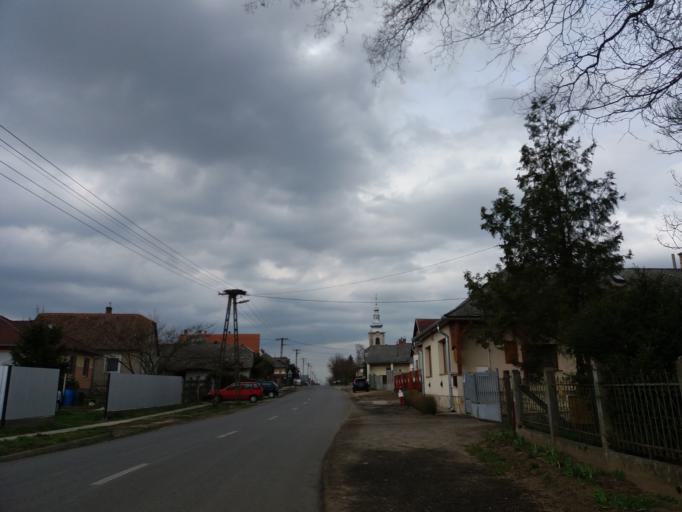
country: HU
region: Szabolcs-Szatmar-Bereg
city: Nyirtass
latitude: 48.1114
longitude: 22.0219
